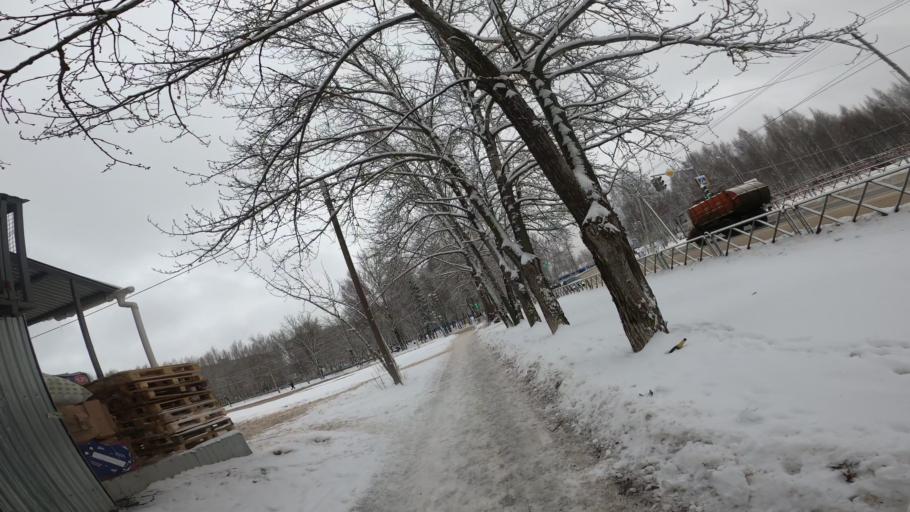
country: RU
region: Jaroslavl
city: Pereslavl'-Zalesskiy
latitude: 56.7503
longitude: 38.8854
